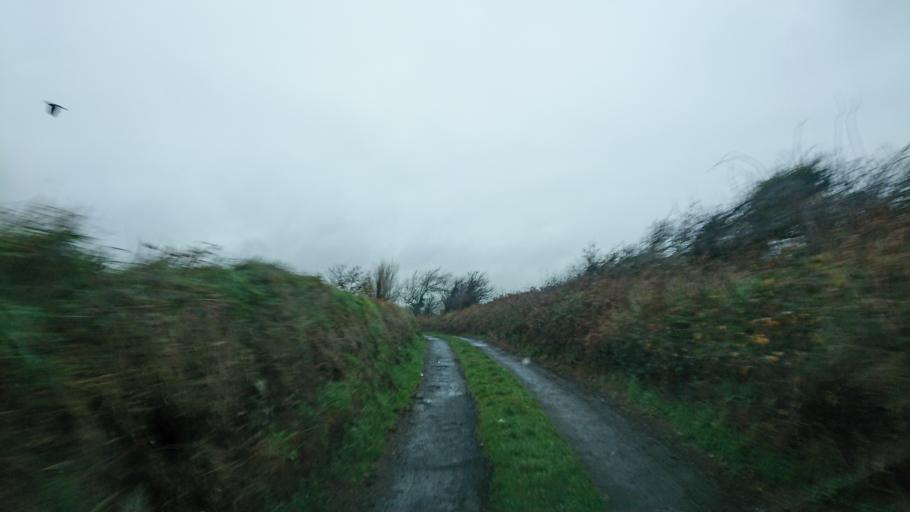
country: IE
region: Munster
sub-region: Waterford
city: Tra Mhor
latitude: 52.1994
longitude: -7.1518
